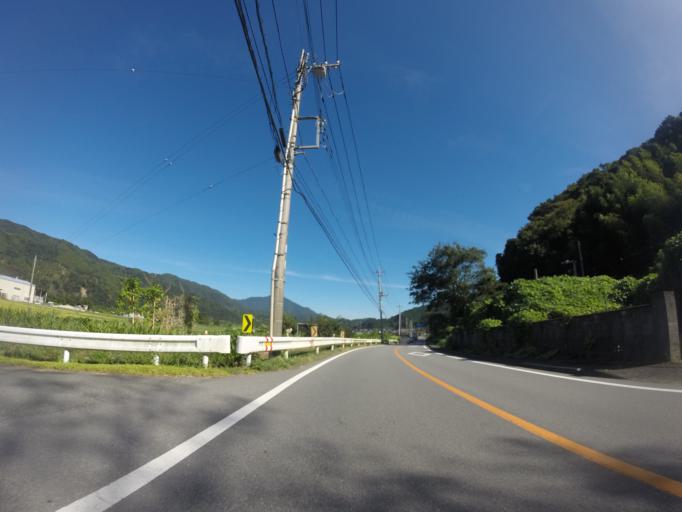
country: JP
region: Shizuoka
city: Fujinomiya
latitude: 35.3241
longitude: 138.4514
